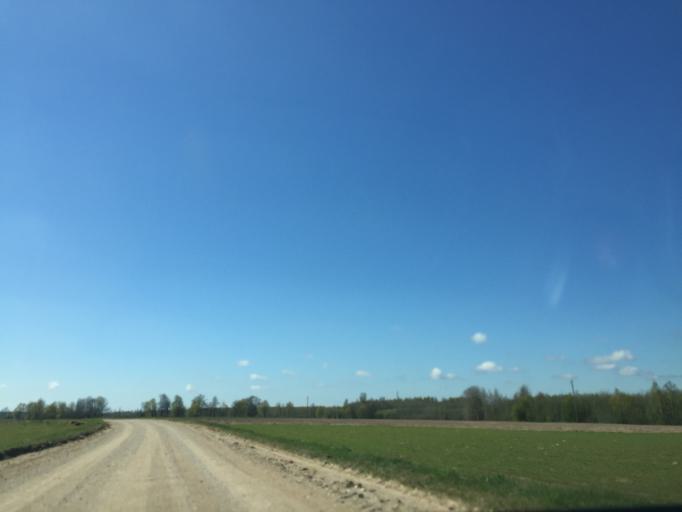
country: LV
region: Smiltene
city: Smiltene
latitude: 57.5550
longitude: 25.8673
